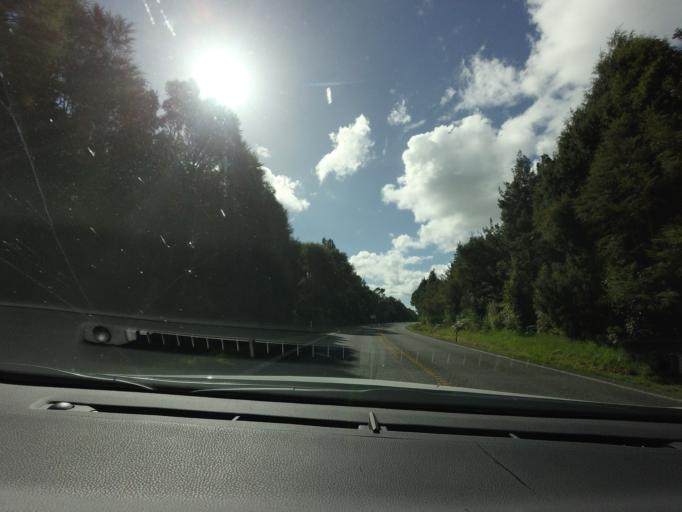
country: NZ
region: Waikato
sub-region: South Waikato District
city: Tokoroa
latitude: -38.0224
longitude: 175.9574
